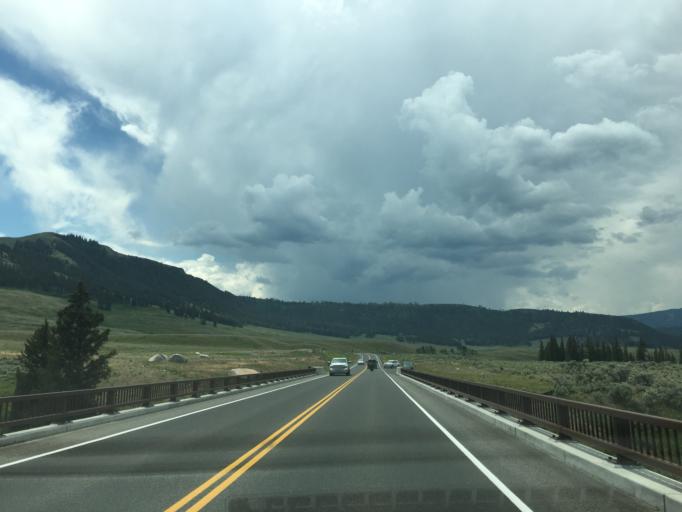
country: US
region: Montana
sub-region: Park County
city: Livingston
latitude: 44.9149
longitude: -110.3233
